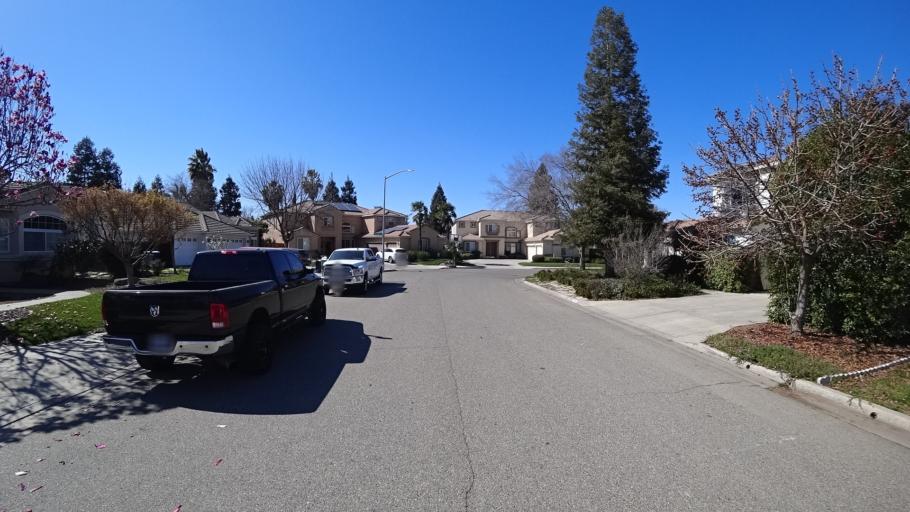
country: US
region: California
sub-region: Fresno County
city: Clovis
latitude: 36.8762
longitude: -119.7375
